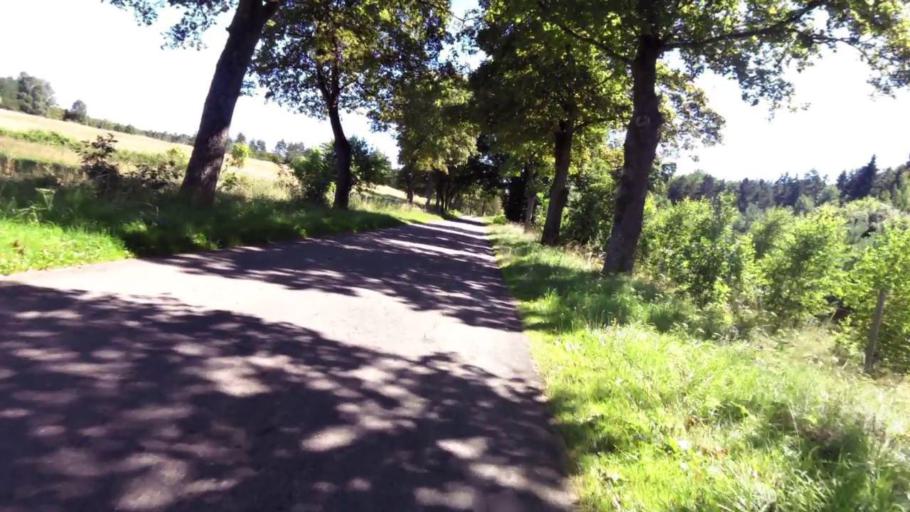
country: PL
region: West Pomeranian Voivodeship
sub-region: Powiat szczecinecki
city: Bialy Bor
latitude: 53.9481
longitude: 16.8479
